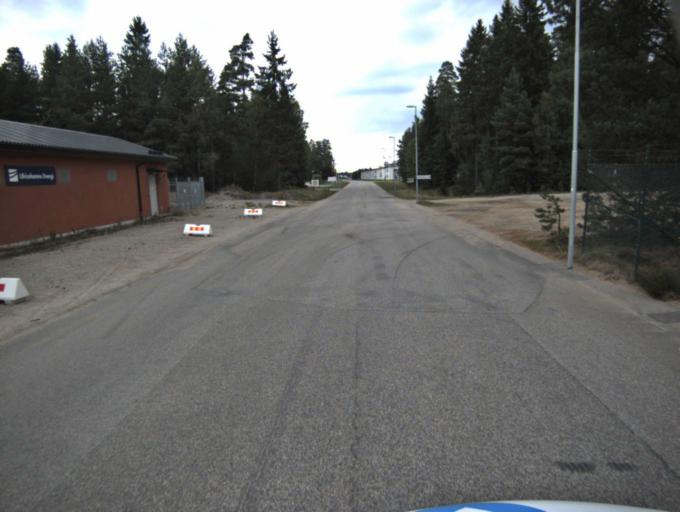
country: SE
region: Vaestra Goetaland
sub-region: Ulricehamns Kommun
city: Ulricehamn
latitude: 57.8300
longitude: 13.4218
